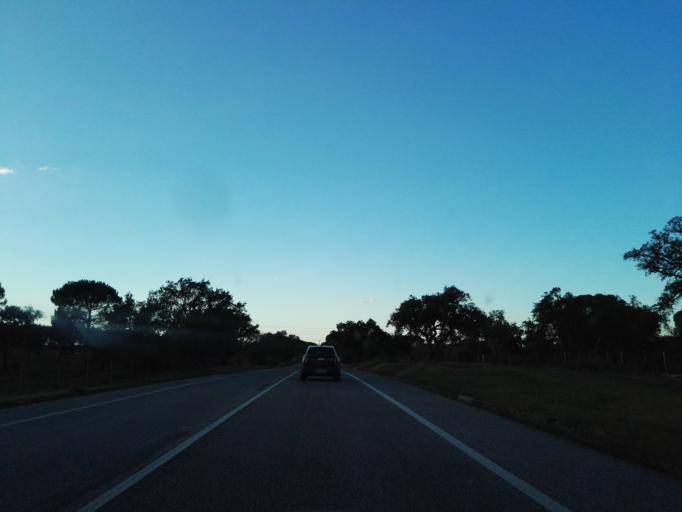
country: PT
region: Santarem
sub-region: Benavente
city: Samora Correia
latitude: 38.8897
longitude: -8.8279
